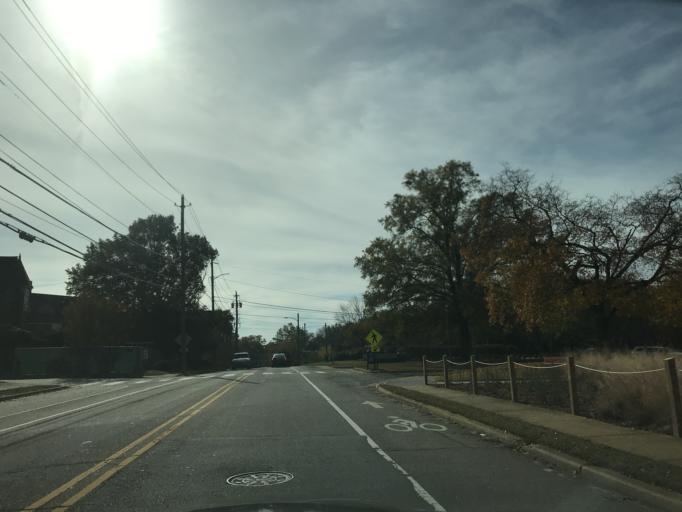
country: US
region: North Carolina
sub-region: Wake County
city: West Raleigh
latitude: 35.7949
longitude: -78.6615
